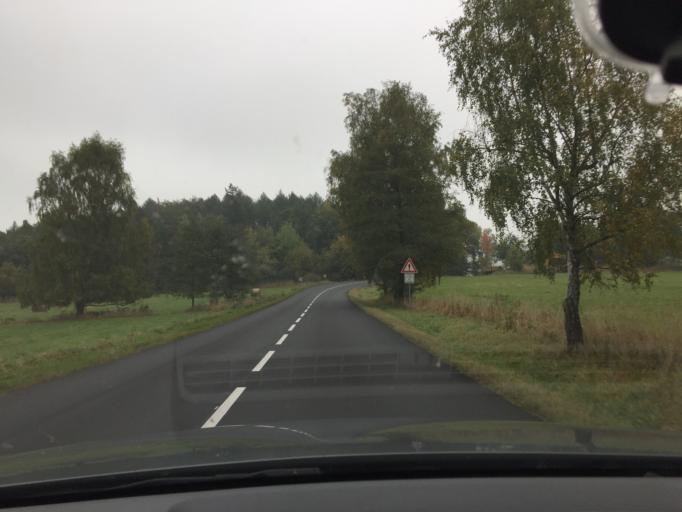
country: CZ
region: Ustecky
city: Libouchec
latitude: 50.7691
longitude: 14.0410
